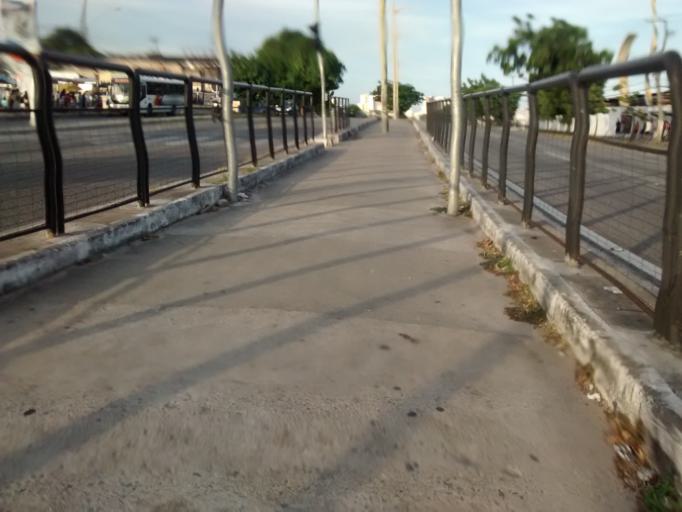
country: BR
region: Ceara
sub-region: Fortaleza
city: Fortaleza
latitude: -3.7386
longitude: -38.5834
